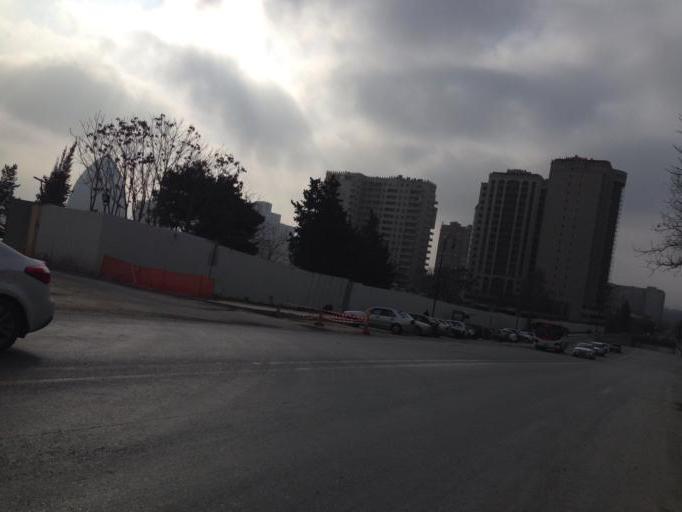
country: AZ
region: Baki
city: Baku
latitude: 40.3974
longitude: 49.8635
